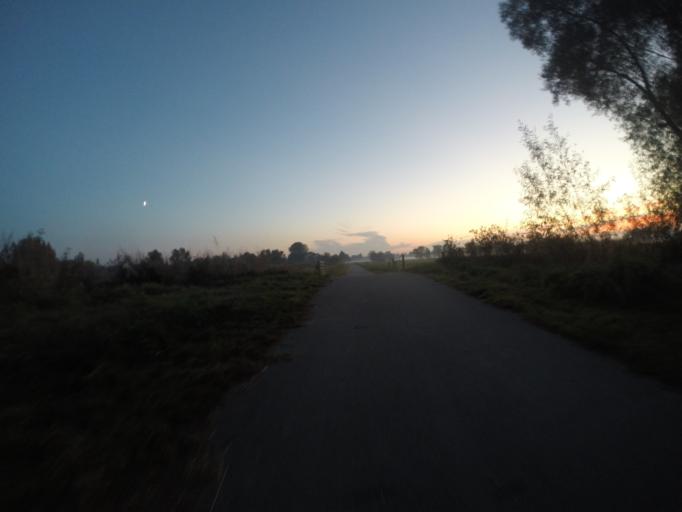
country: DK
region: Capital Region
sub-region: Vallensbaek Kommune
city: Vallensbaek
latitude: 55.6320
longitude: 12.3604
